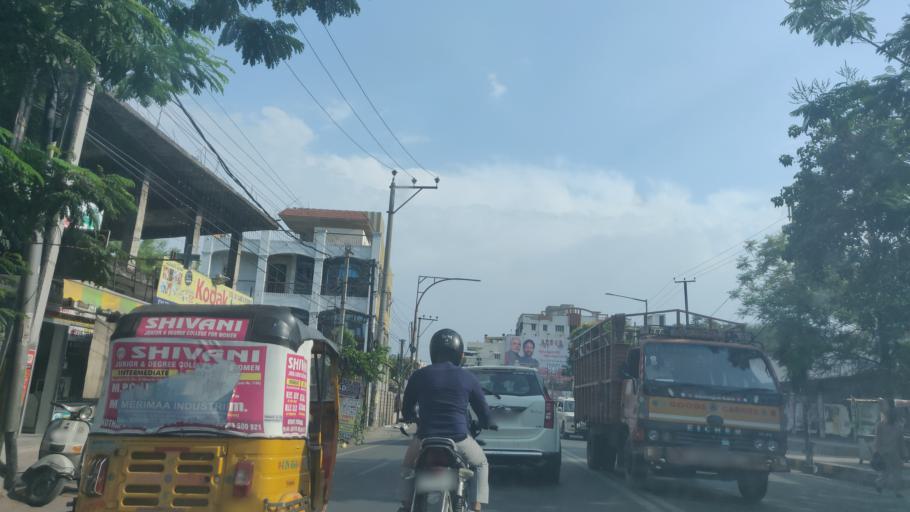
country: IN
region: Telangana
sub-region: Rangareddi
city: Gaddi Annaram
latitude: 17.3923
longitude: 78.5109
